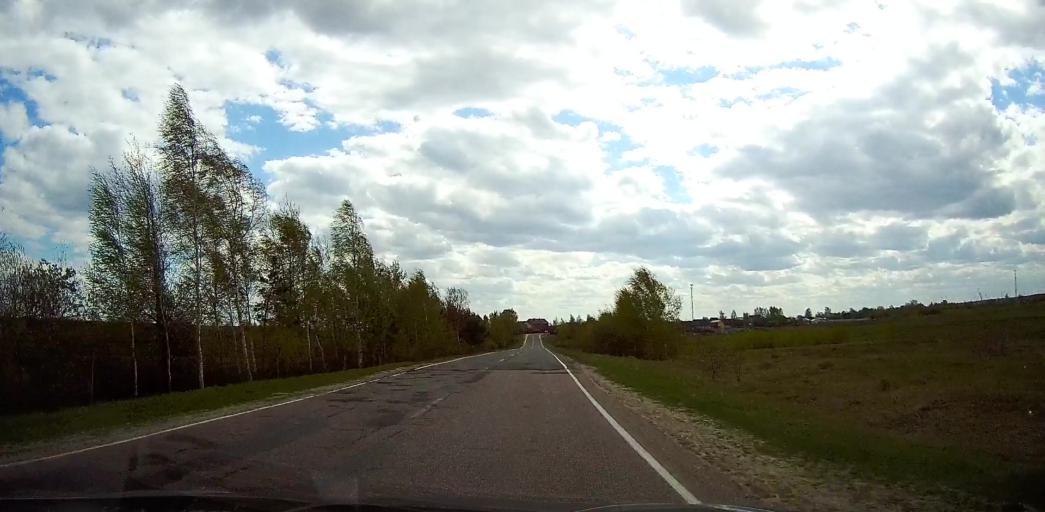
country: RU
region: Moskovskaya
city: Davydovo
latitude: 55.6345
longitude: 38.7463
